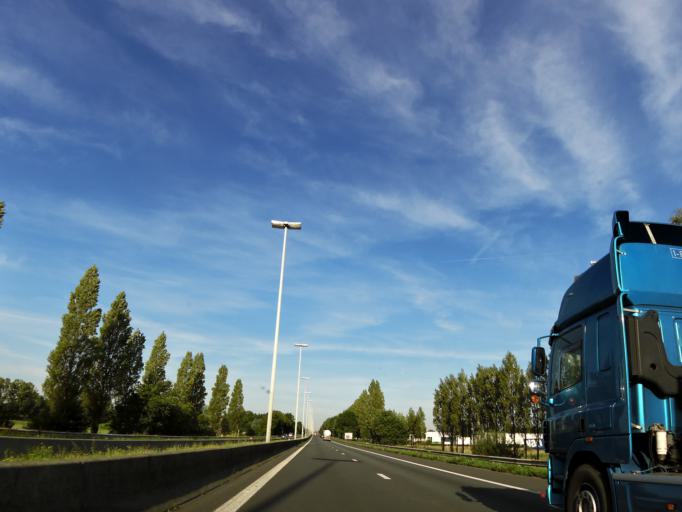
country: BE
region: Flanders
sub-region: Provincie Limburg
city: Tessenderlo
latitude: 51.0967
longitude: 5.0788
